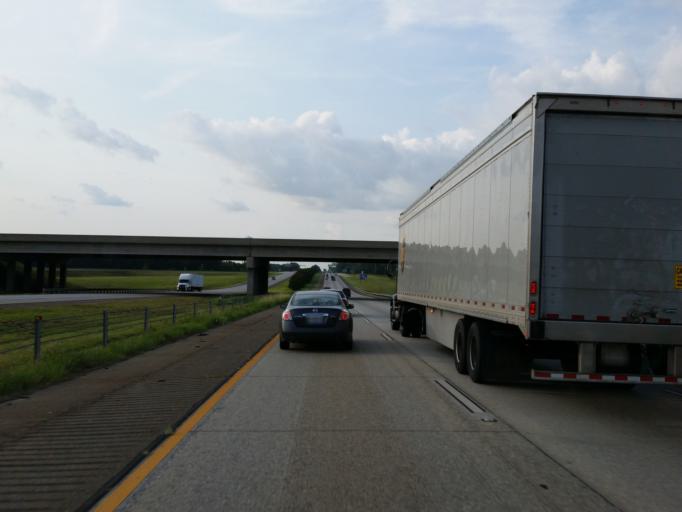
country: US
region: Georgia
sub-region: Houston County
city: Centerville
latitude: 32.5855
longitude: -83.7431
